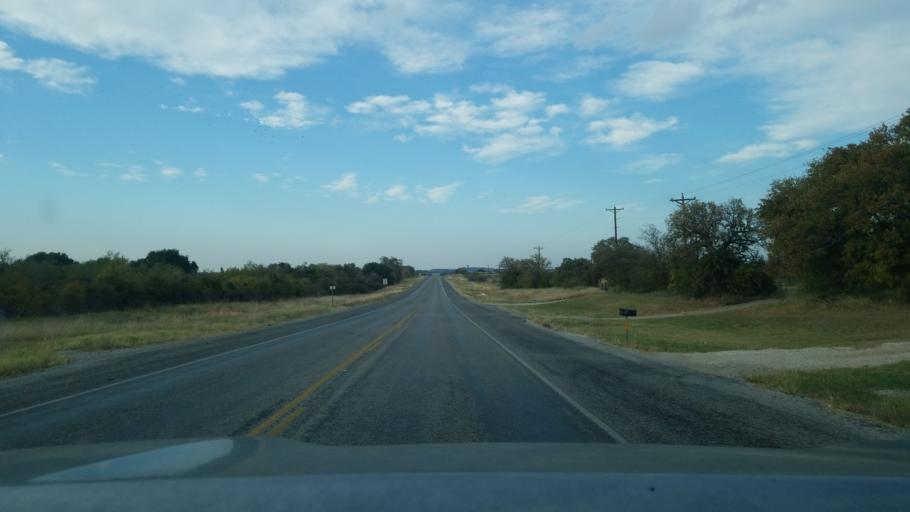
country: US
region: Texas
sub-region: Brown County
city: Lake Brownwood
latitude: 31.9833
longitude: -98.9207
